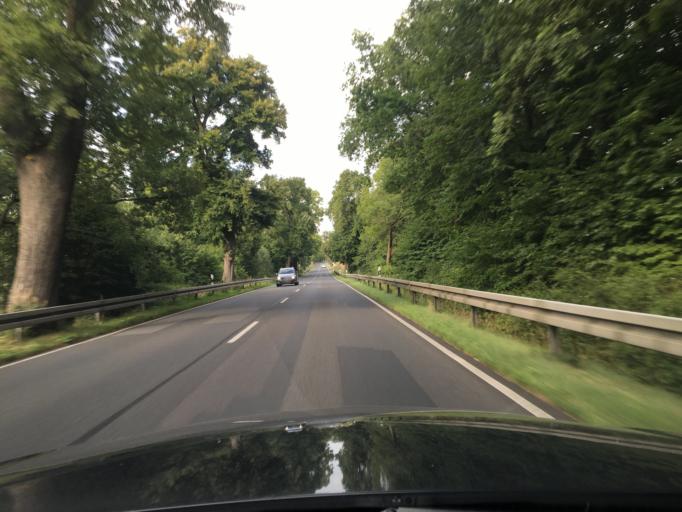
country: DE
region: Mecklenburg-Vorpommern
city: Wustrow
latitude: 53.4183
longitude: 13.1344
